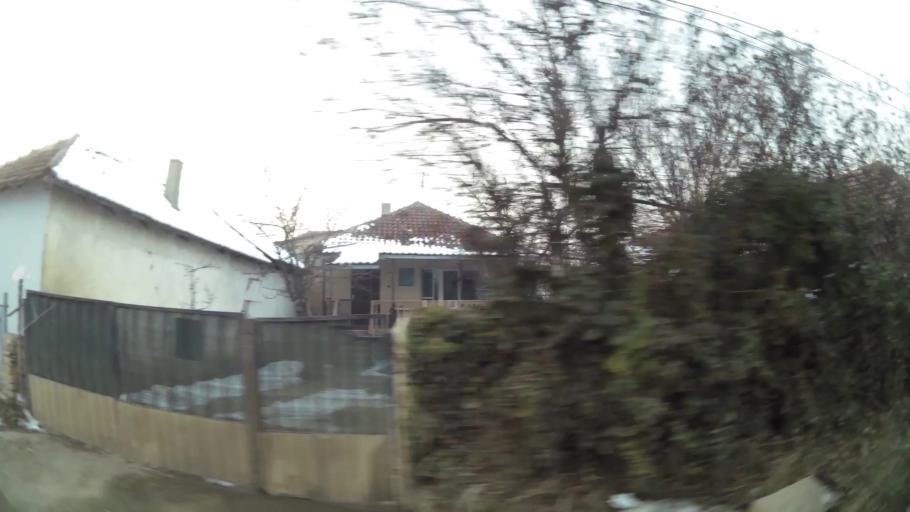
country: MK
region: Suto Orizari
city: Suto Orizare
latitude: 42.0353
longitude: 21.4098
